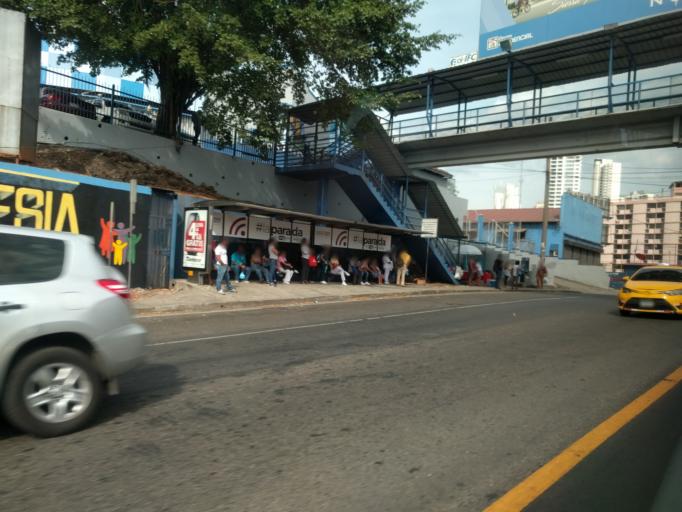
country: PA
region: Panama
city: Panama
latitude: 8.9774
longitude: -79.5350
